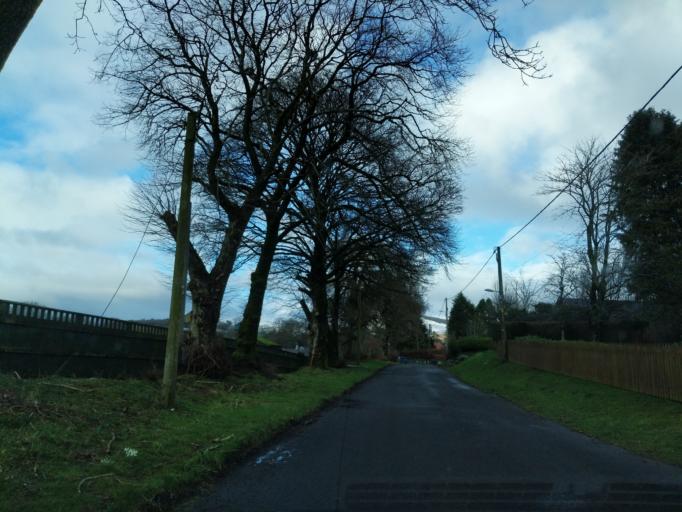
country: GB
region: Scotland
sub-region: Dumfries and Galloway
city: Moffat
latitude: 55.3247
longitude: -3.4308
